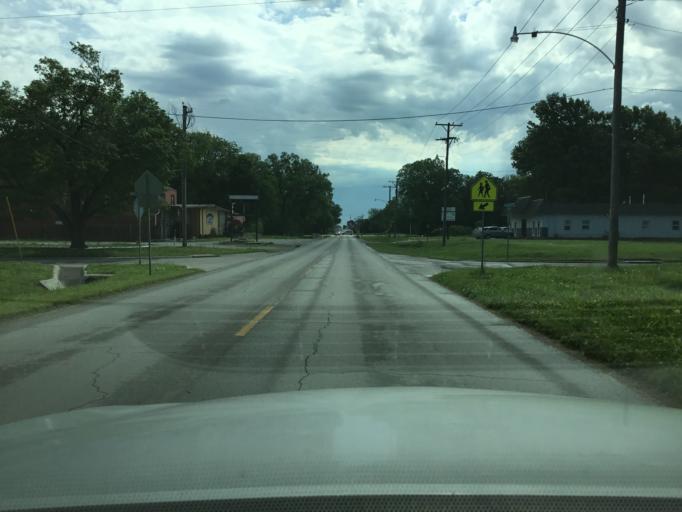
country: US
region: Kansas
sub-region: Montgomery County
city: Coffeyville
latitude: 37.0363
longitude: -95.6502
